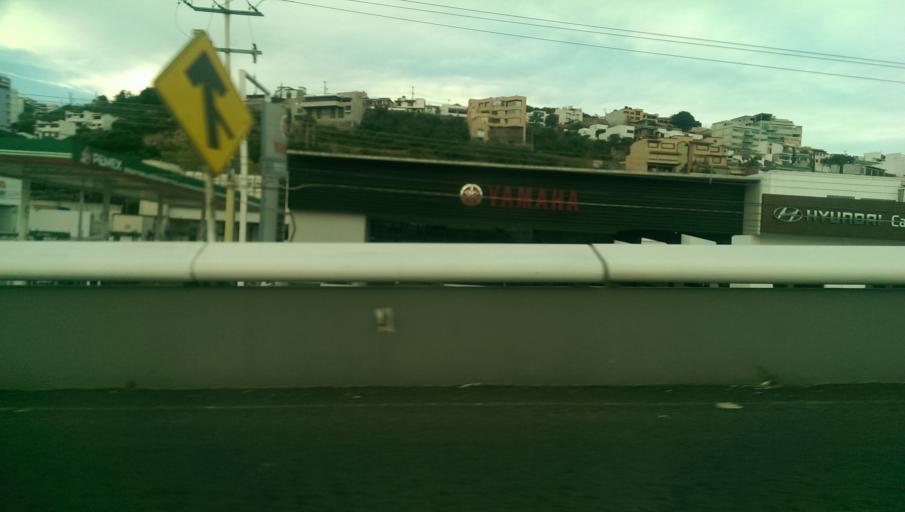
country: MX
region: Queretaro
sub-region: Queretaro
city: Santiago de Queretaro
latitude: 20.5908
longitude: -100.3663
